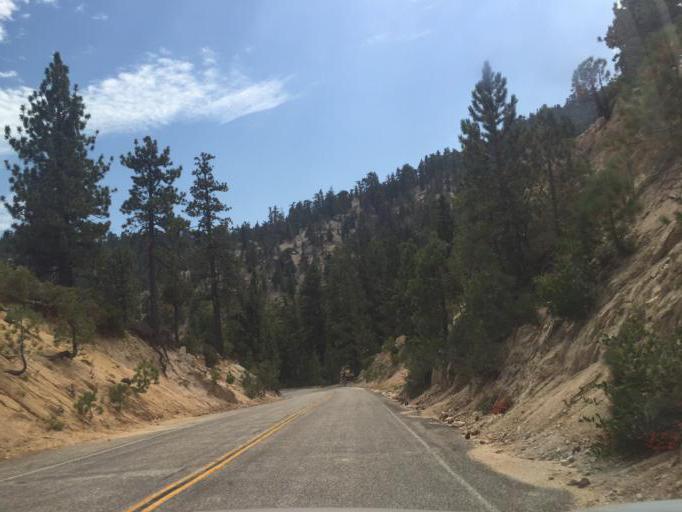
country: US
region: California
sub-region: Los Angeles County
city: Littlerock
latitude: 34.3443
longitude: -117.9210
